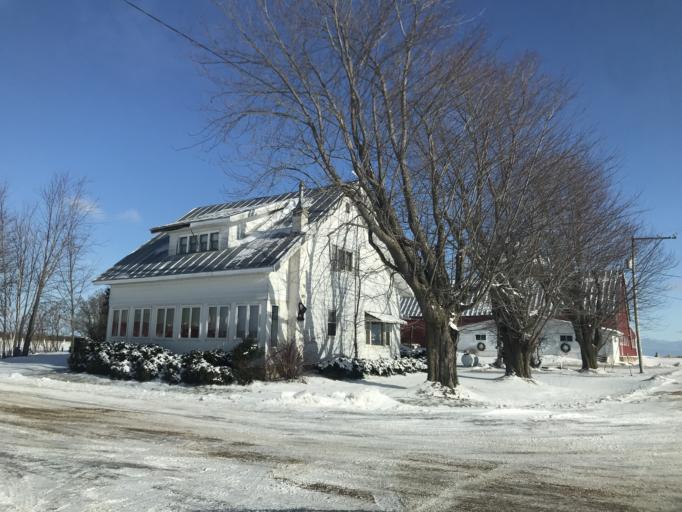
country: US
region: Wisconsin
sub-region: Kewaunee County
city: Luxemburg
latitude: 44.6974
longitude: -87.6004
